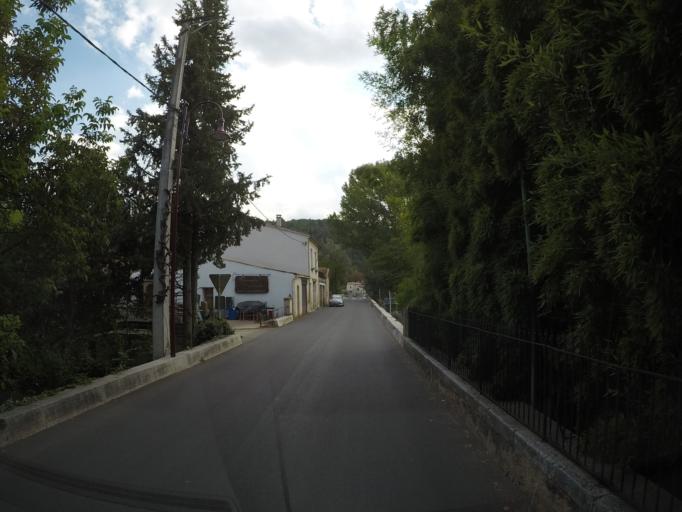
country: FR
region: Provence-Alpes-Cote d'Azur
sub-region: Departement des Alpes-de-Haute-Provence
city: Riez
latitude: 43.8177
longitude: 6.0904
